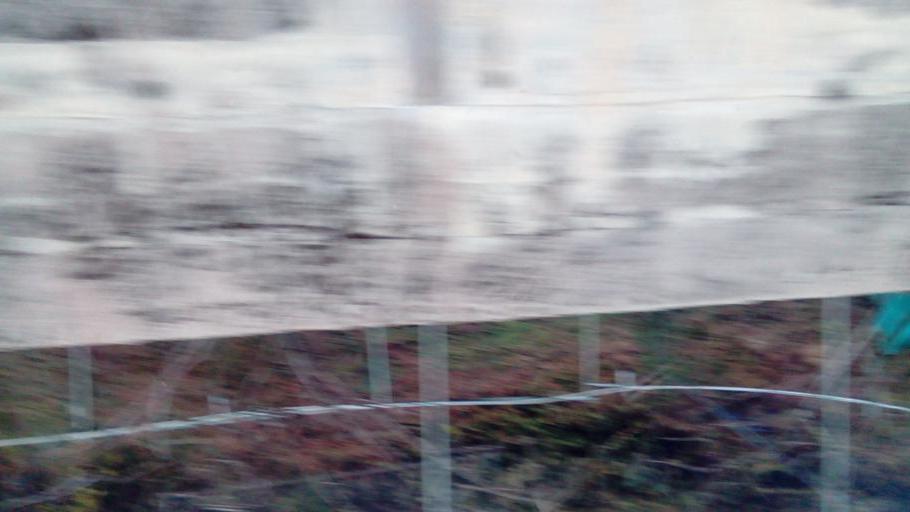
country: TW
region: Taiwan
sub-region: Hualien
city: Hualian
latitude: 24.3449
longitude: 121.3179
